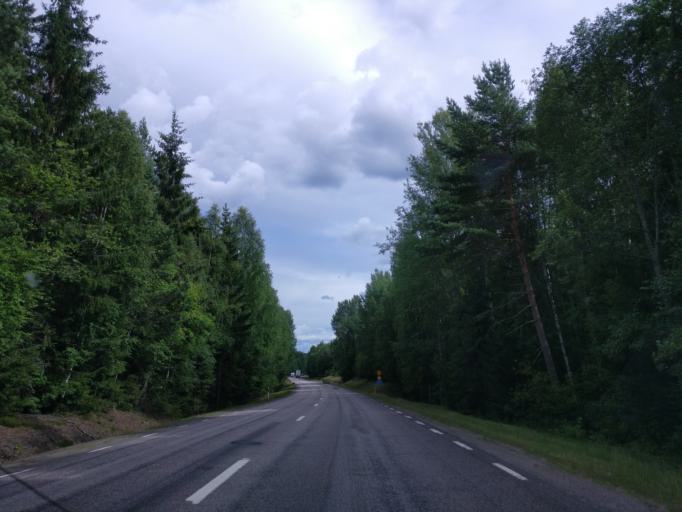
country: SE
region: Vaermland
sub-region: Hagfors Kommun
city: Ekshaerad
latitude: 60.1606
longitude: 13.5063
